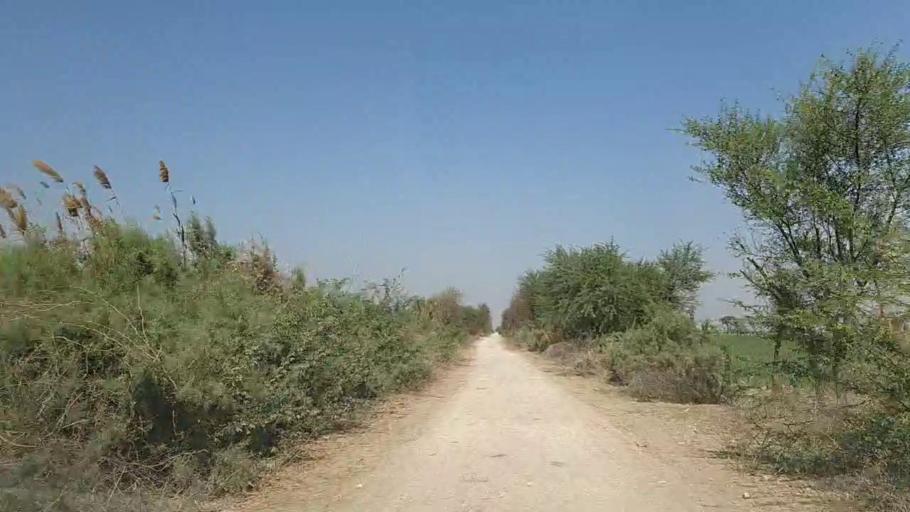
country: PK
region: Sindh
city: Samaro
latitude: 25.1934
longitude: 69.4041
